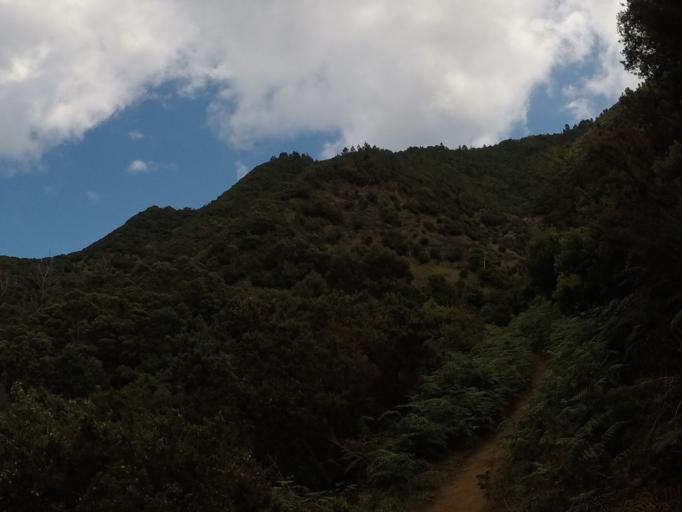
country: PT
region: Madeira
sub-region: Machico
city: Canical
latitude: 32.7519
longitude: -16.7709
